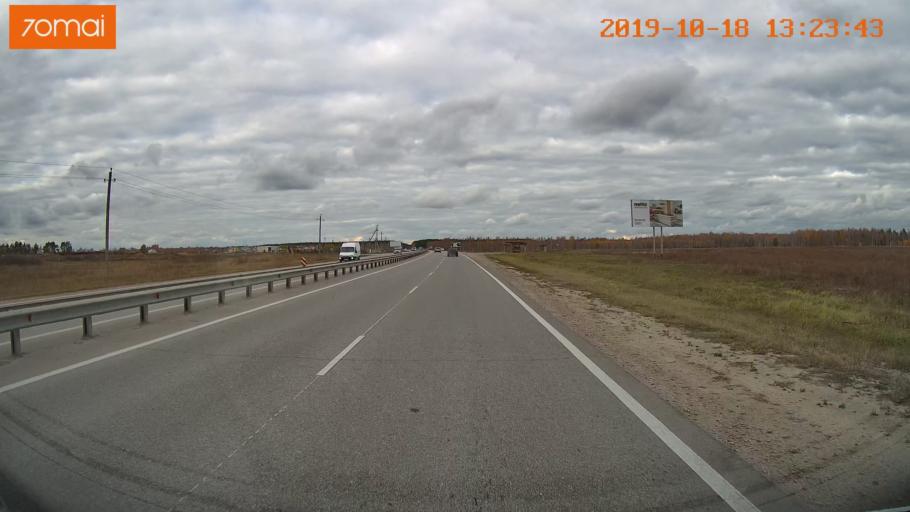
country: RU
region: Rjazan
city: Polyany
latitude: 54.7203
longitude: 39.8480
